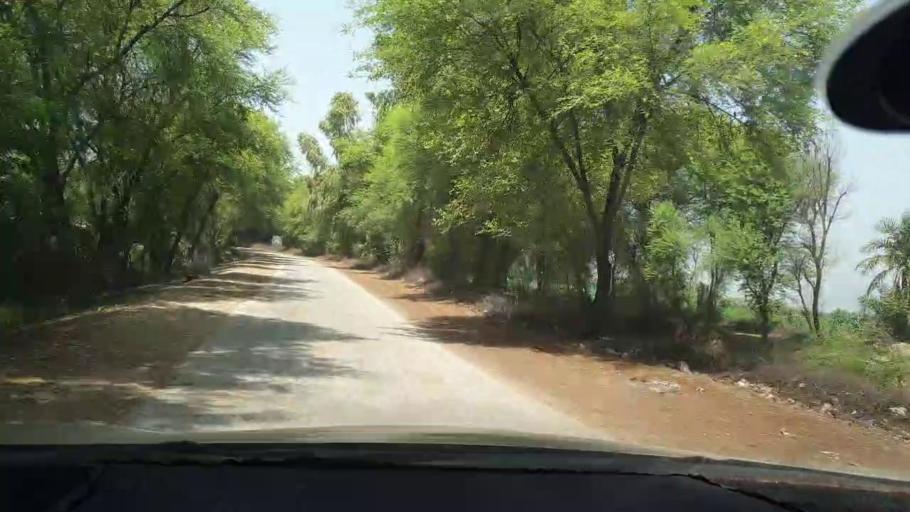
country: PK
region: Sindh
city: Kambar
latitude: 27.6564
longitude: 67.9604
